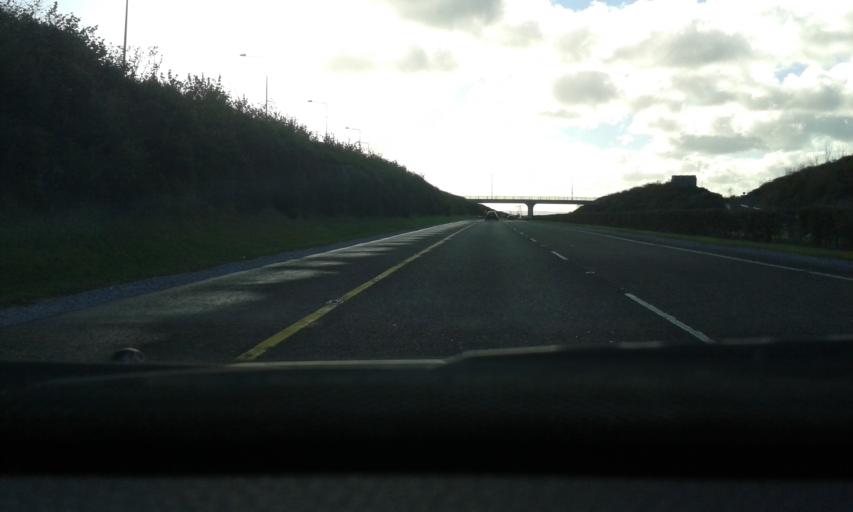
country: IE
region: Munster
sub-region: County Cork
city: Watergrasshill
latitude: 52.0098
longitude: -8.3399
